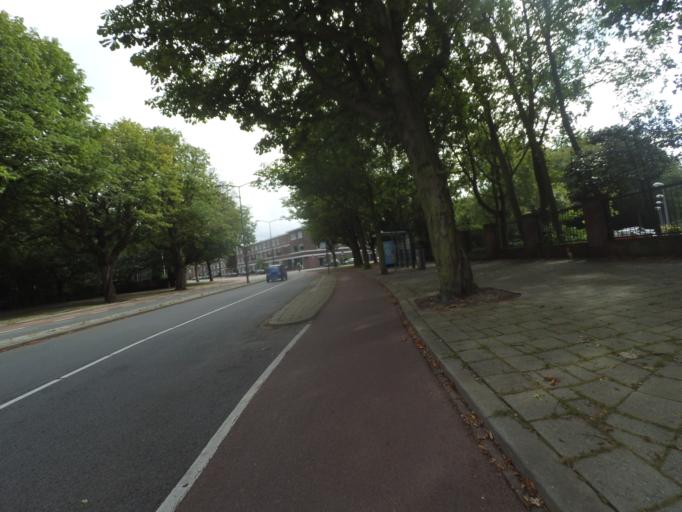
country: NL
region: South Holland
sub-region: Gemeente Den Haag
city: The Hague
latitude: 52.0970
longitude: 4.3115
